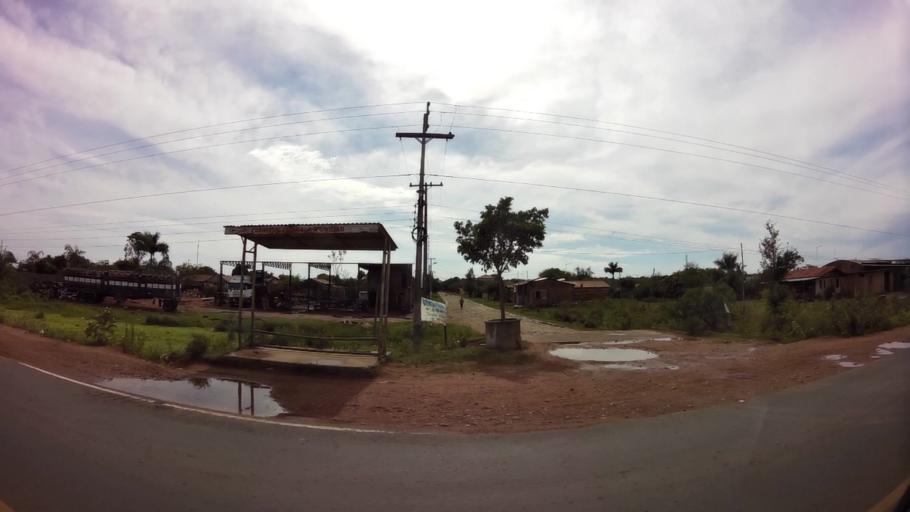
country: PY
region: Central
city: Limpio
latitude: -25.1321
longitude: -57.4803
